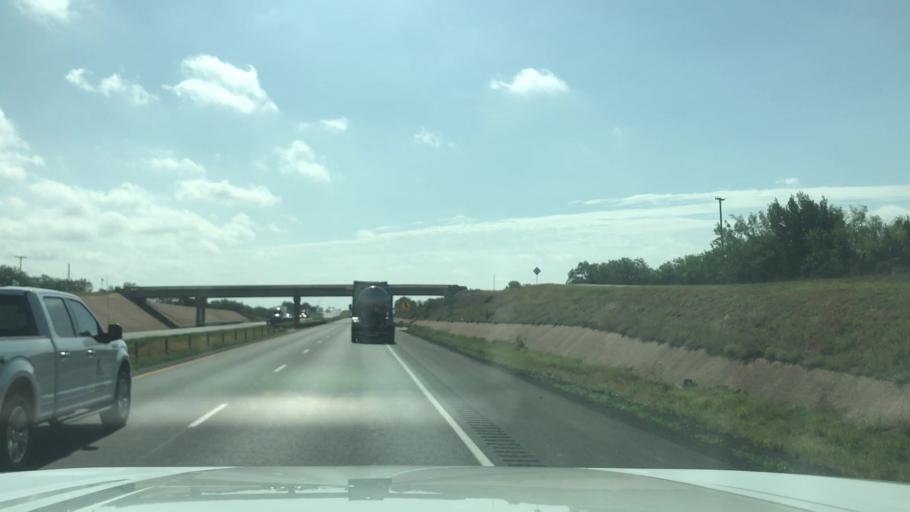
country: US
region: Texas
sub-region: Nolan County
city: Sweetwater
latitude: 32.4890
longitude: -100.2180
